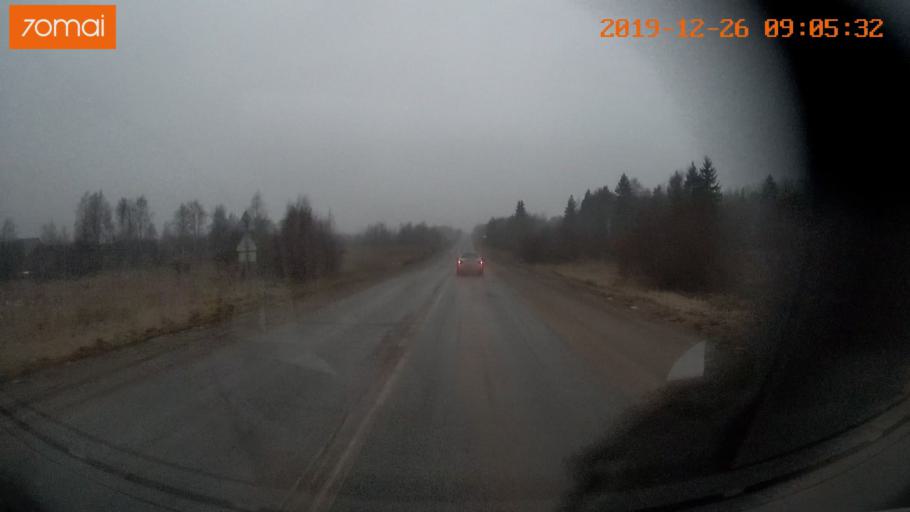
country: RU
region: Vologda
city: Gryazovets
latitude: 58.8265
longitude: 40.2575
